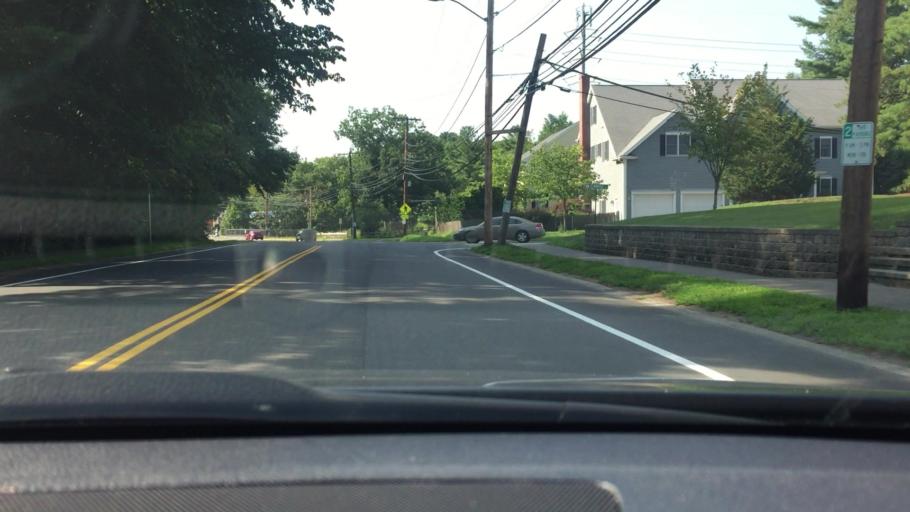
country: US
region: Massachusetts
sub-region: Norfolk County
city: Needham
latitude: 42.2747
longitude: -71.2135
